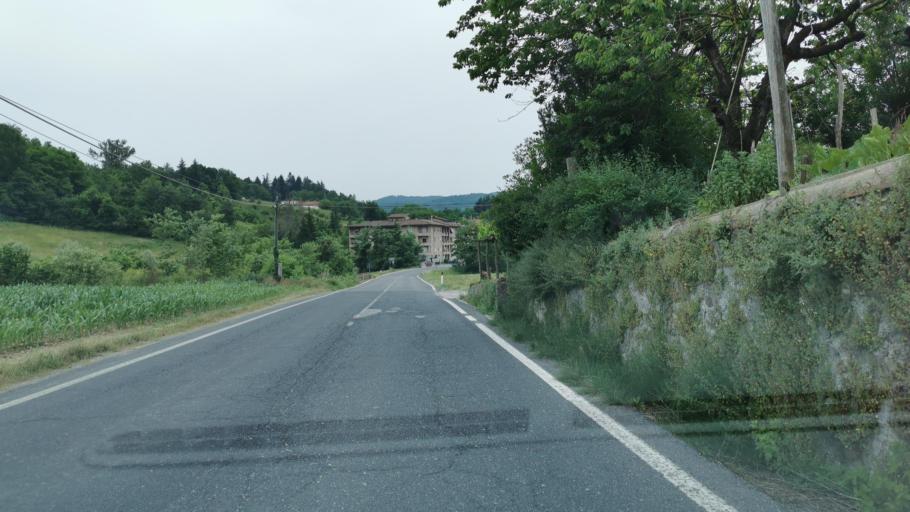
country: IT
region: Piedmont
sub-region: Provincia di Cuneo
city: Ceva
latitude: 44.3906
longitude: 8.0449
